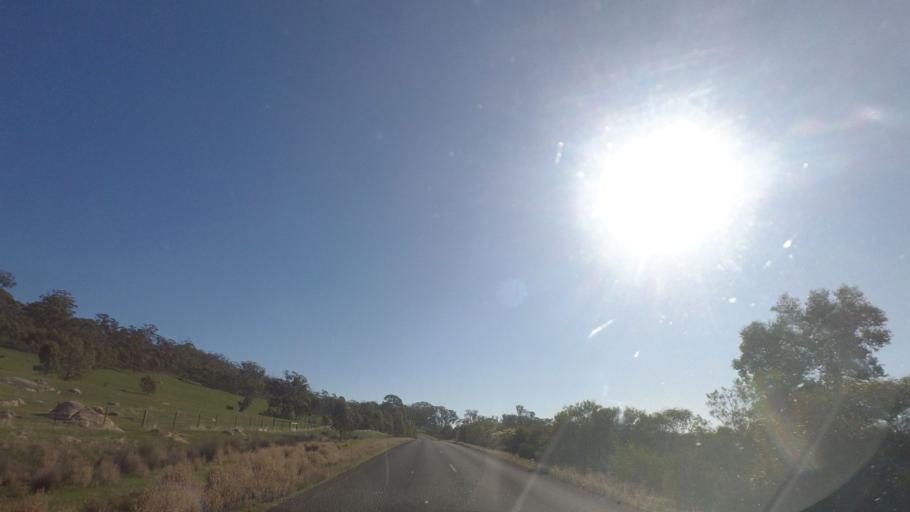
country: AU
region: Victoria
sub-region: Mount Alexander
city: Castlemaine
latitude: -37.0369
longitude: 144.2776
